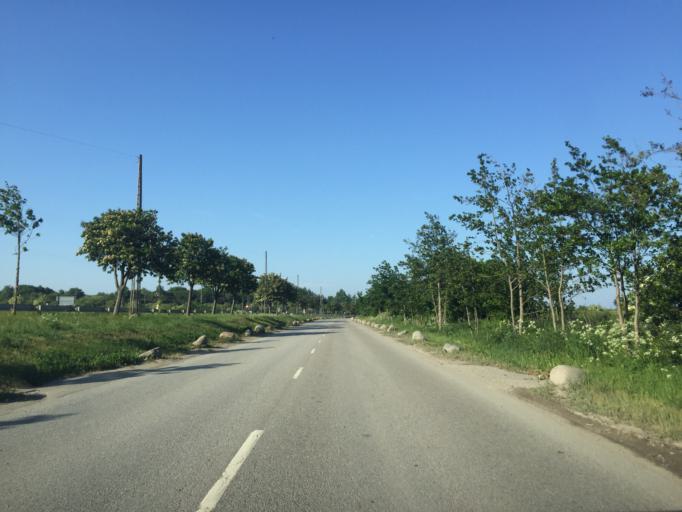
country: DK
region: Capital Region
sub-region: Kobenhavn
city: Copenhagen
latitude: 55.6390
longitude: 12.5564
